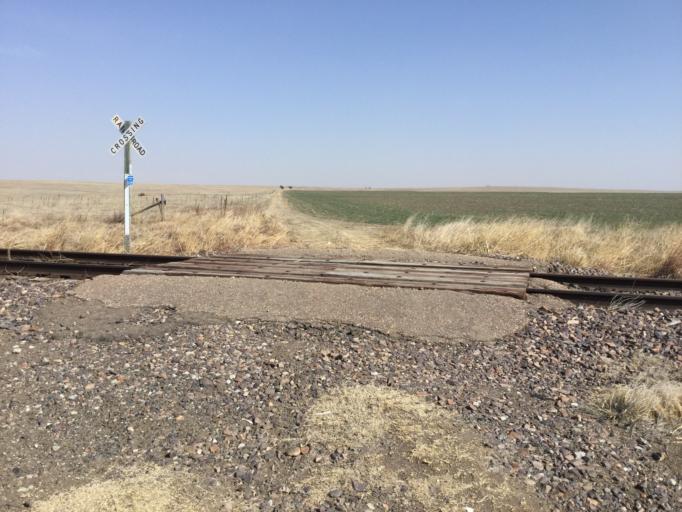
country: US
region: Kansas
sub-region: Rush County
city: La Crosse
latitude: 38.5477
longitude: -99.4202
